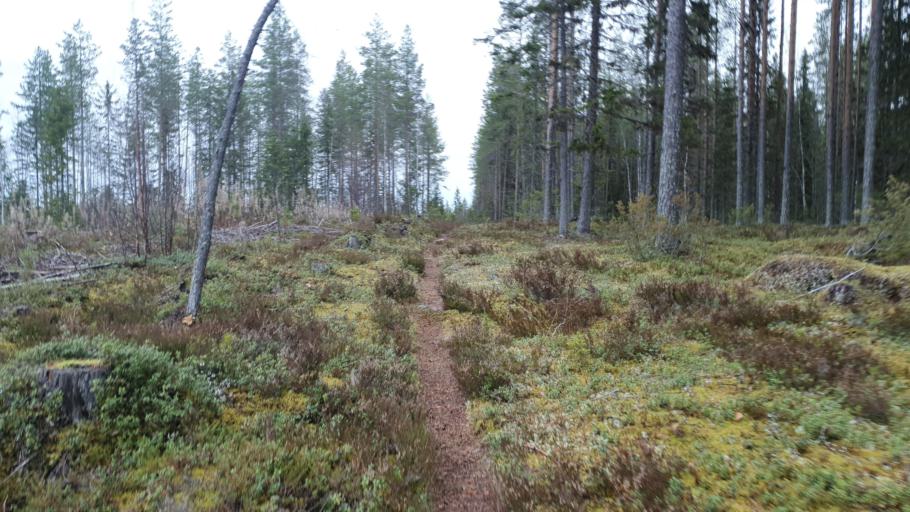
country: FI
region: Kainuu
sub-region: Kehys-Kainuu
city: Kuhmo
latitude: 64.1335
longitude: 29.3909
